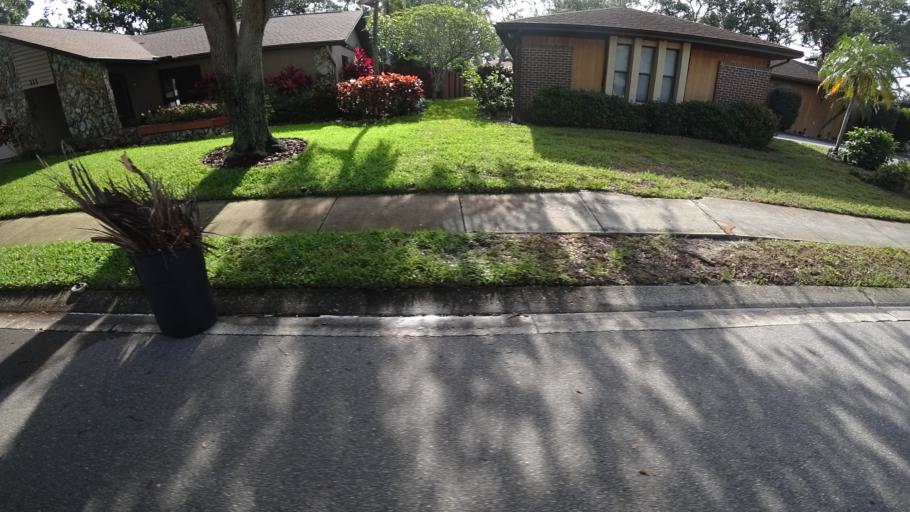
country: US
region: Florida
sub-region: Manatee County
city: West Bradenton
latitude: 27.5022
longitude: -82.6379
